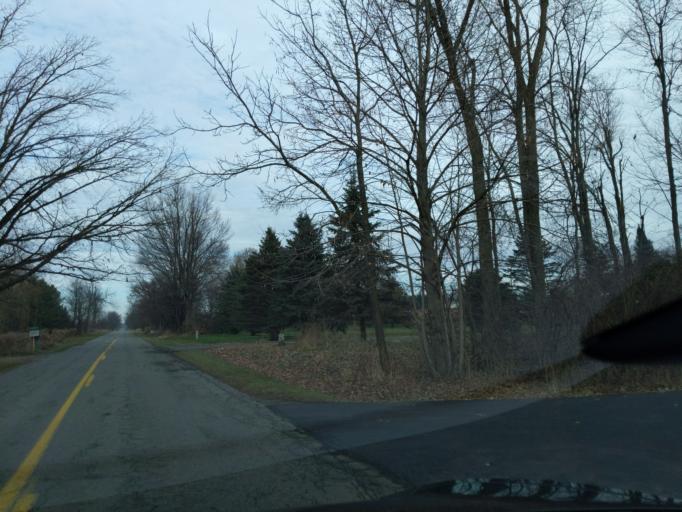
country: US
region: Michigan
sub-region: Ingham County
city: Leslie
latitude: 42.4985
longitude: -84.5024
